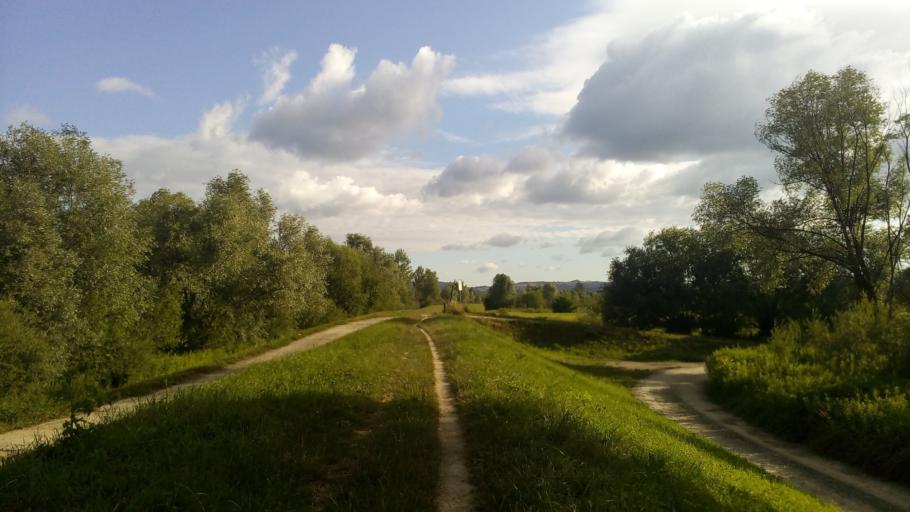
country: PL
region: Lesser Poland Voivodeship
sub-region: Powiat nowosadecki
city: Chelmiec
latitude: 49.6031
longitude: 20.6710
